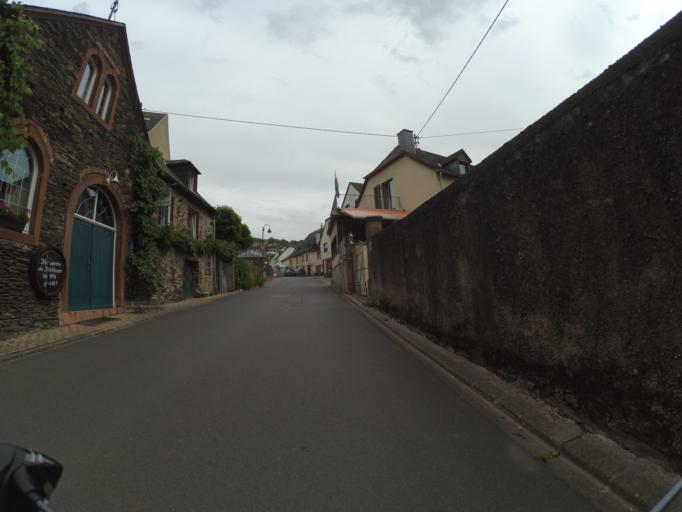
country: DE
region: Rheinland-Pfalz
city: Neumagen-Dhron
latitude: 49.8508
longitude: 6.8937
